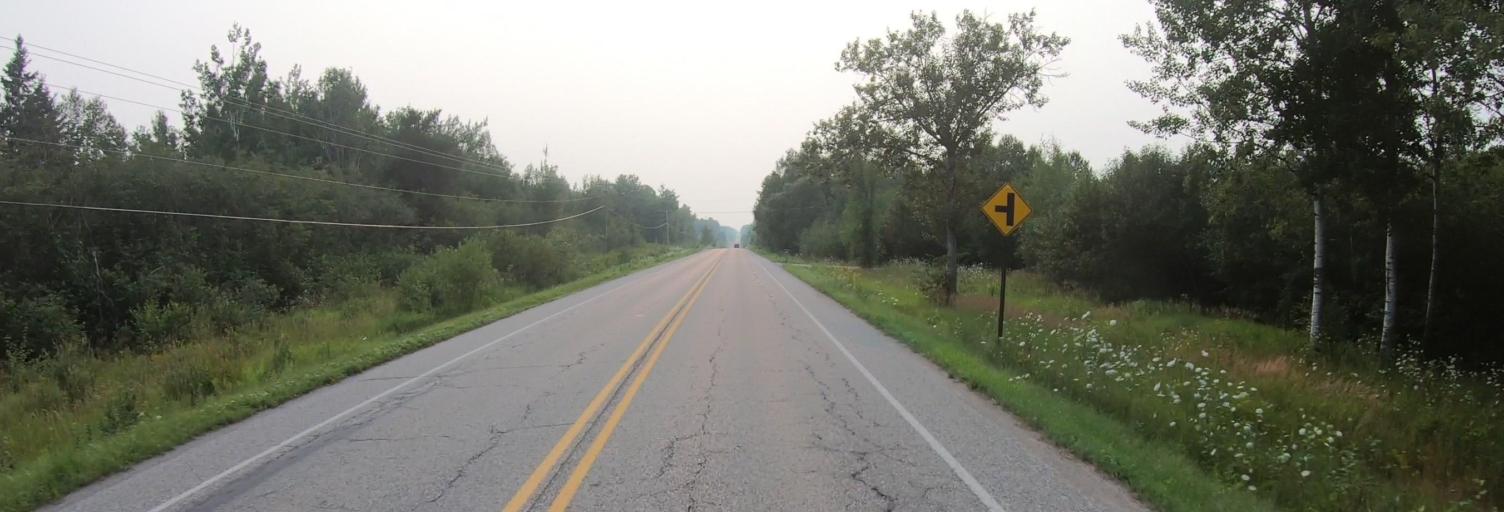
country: US
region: Michigan
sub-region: Chippewa County
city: Sault Ste. Marie
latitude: 46.4189
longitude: -84.4609
